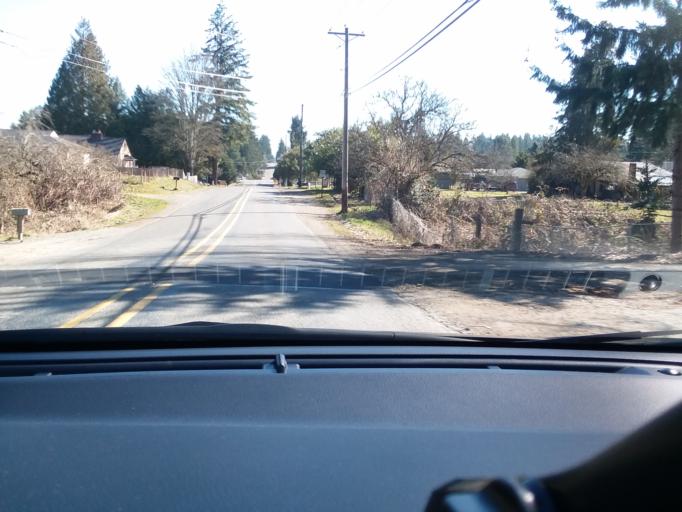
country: US
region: Washington
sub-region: Pierce County
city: Summit
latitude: 47.1700
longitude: -122.3608
